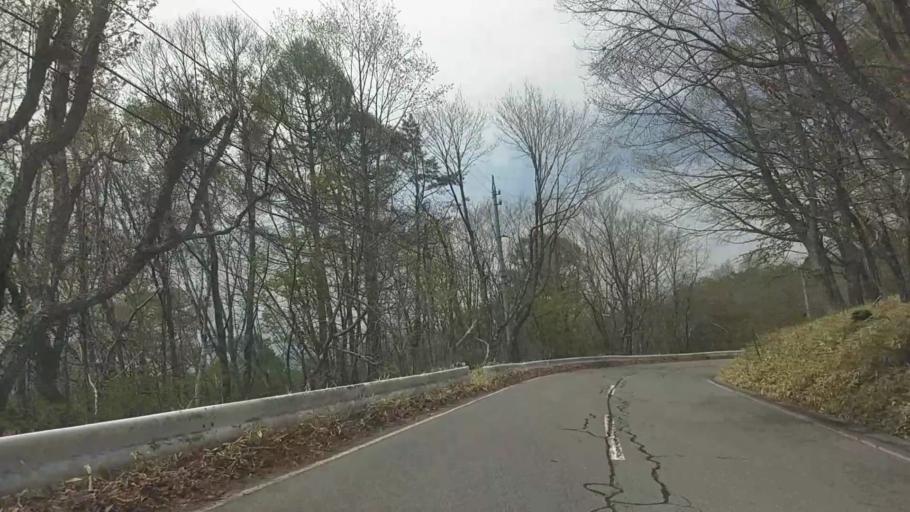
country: JP
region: Nagano
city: Chino
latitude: 36.0459
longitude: 138.3025
